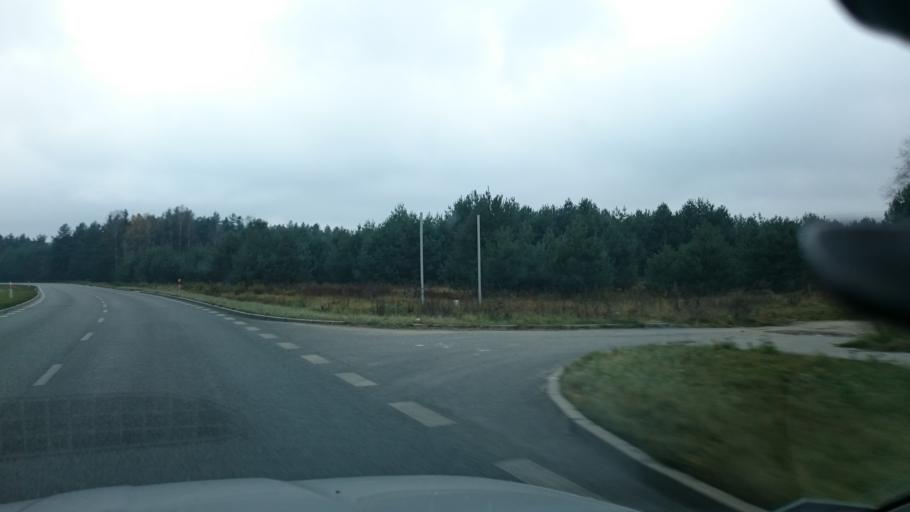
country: PL
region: Swietokrzyskie
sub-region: Powiat konecki
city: Konskie
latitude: 51.1527
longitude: 20.3623
